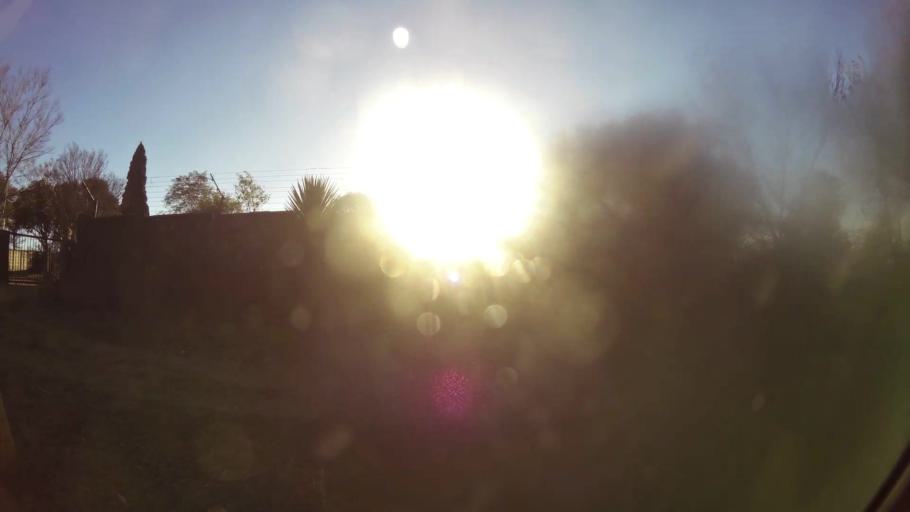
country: ZA
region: Gauteng
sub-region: City of Johannesburg Metropolitan Municipality
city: Midrand
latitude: -26.0117
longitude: 28.1342
